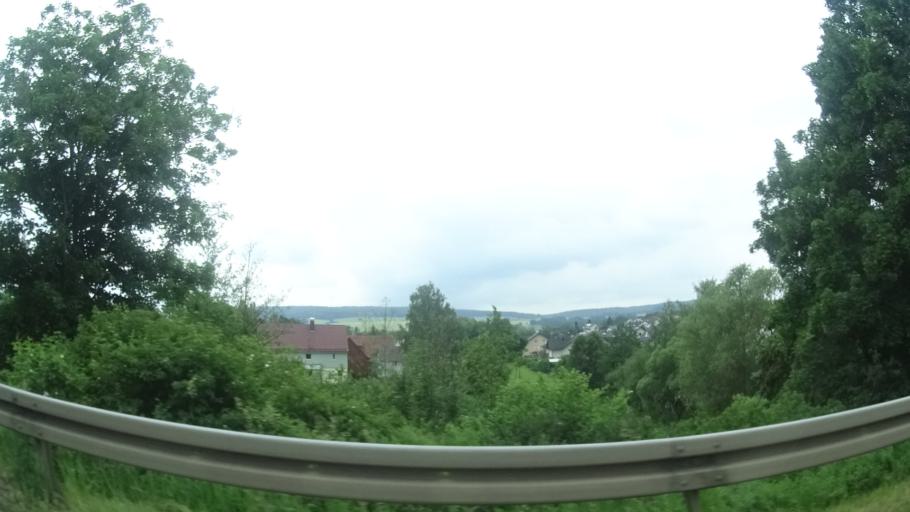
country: DE
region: Hesse
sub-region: Regierungsbezirk Kassel
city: Grossenluder
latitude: 50.5743
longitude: 9.5796
